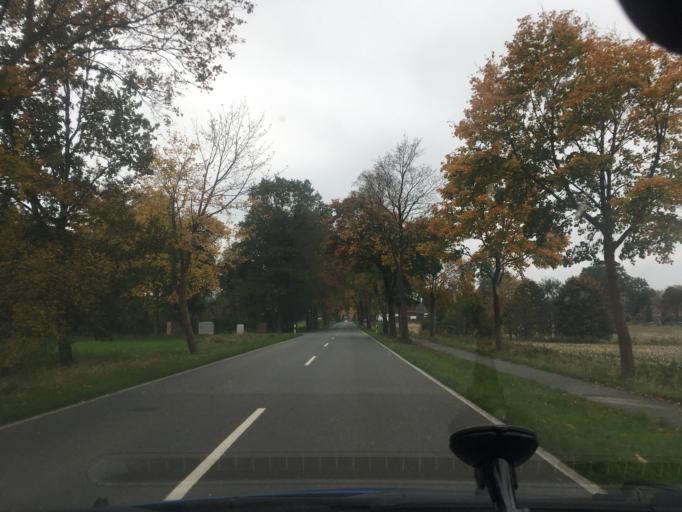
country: DE
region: Lower Saxony
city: Bispingen
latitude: 53.0889
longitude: 10.0107
